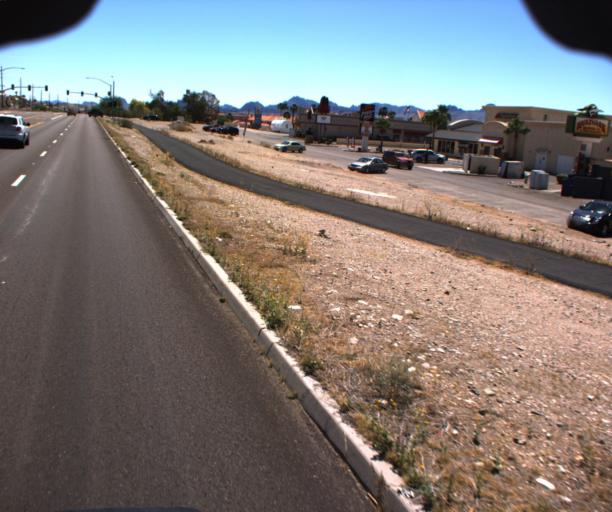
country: US
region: Arizona
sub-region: Mohave County
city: Lake Havasu City
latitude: 34.4692
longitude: -114.3408
